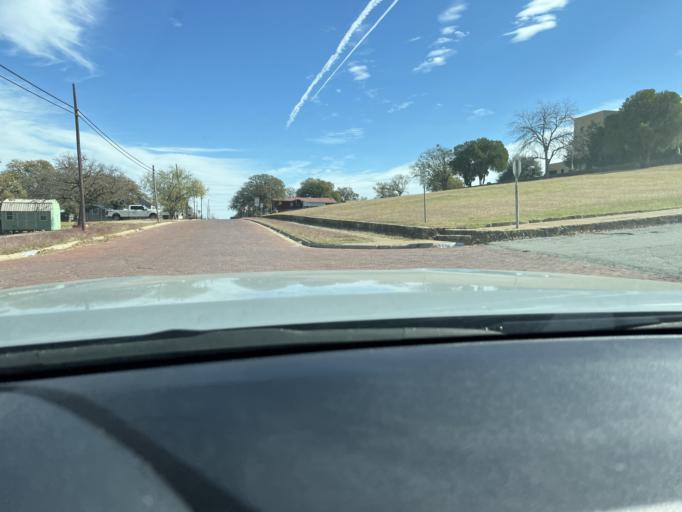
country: US
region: Texas
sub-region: Eastland County
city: Eastland
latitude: 32.3995
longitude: -98.8283
